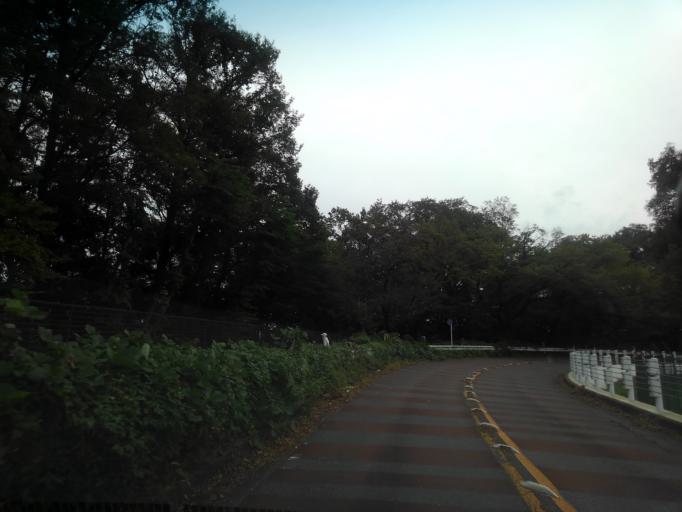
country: JP
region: Tokyo
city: Higashimurayama-shi
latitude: 35.7685
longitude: 139.4380
